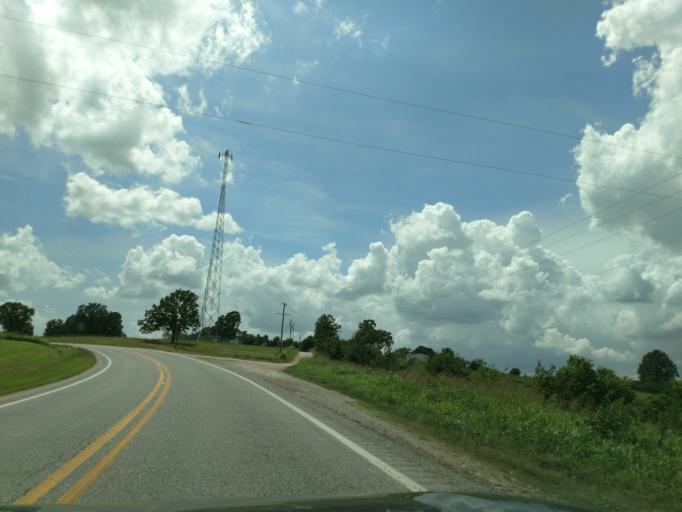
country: US
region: Arkansas
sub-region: Boone County
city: Harrison
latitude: 36.2111
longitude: -92.9308
